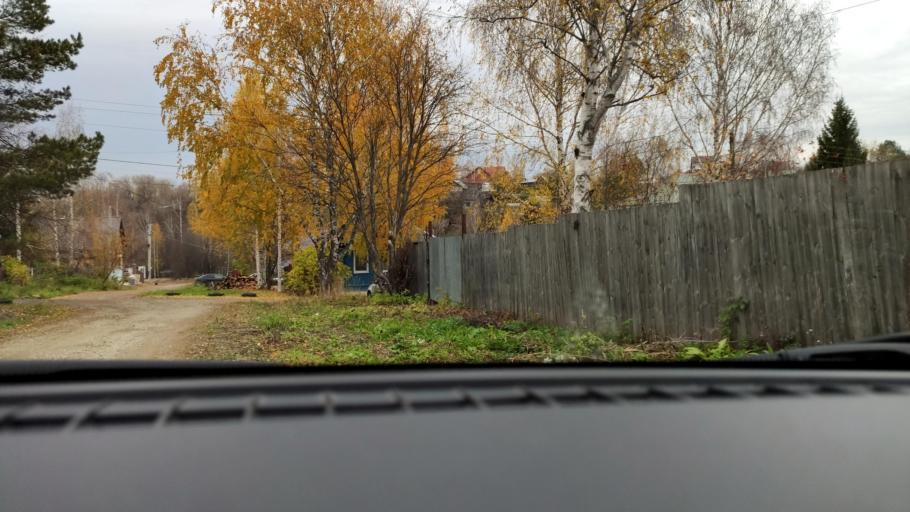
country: RU
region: Perm
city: Perm
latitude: 58.0216
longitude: 56.3199
